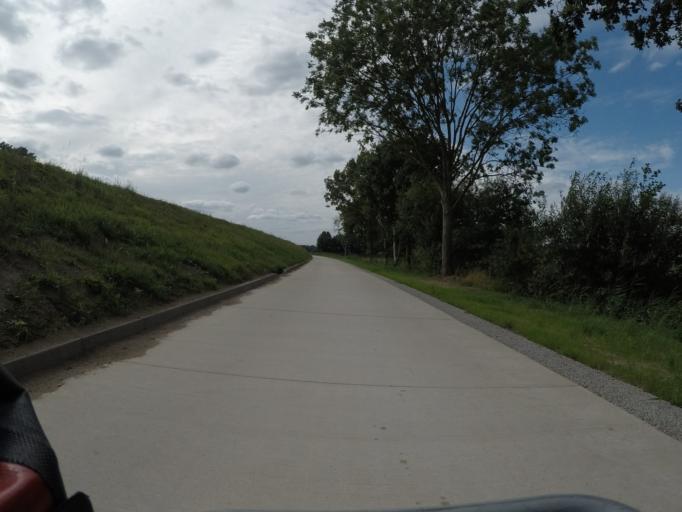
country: DE
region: Lower Saxony
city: Handorf
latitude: 53.3534
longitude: 10.3689
